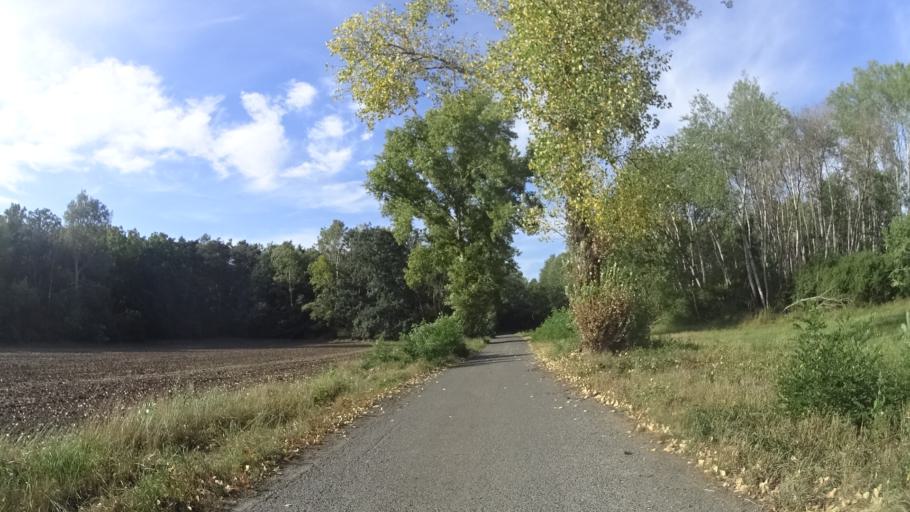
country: AT
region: Lower Austria
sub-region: Politischer Bezirk Mistelbach
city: Rabensburg
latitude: 48.5968
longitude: 16.9499
